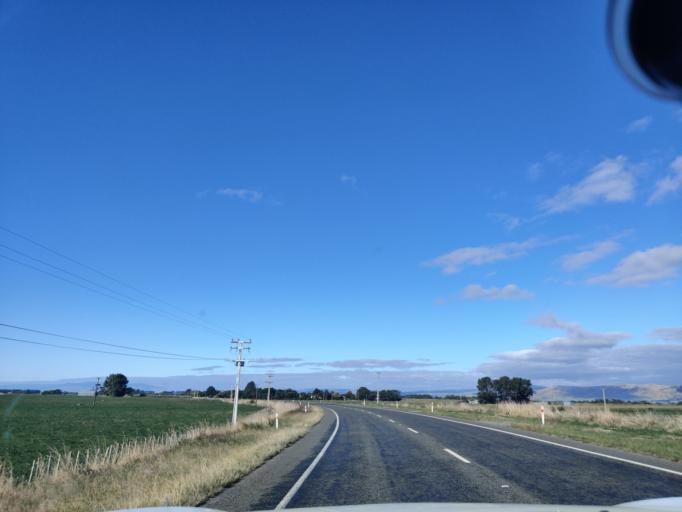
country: NZ
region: Manawatu-Wanganui
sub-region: Horowhenua District
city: Foxton
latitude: -40.4256
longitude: 175.4566
